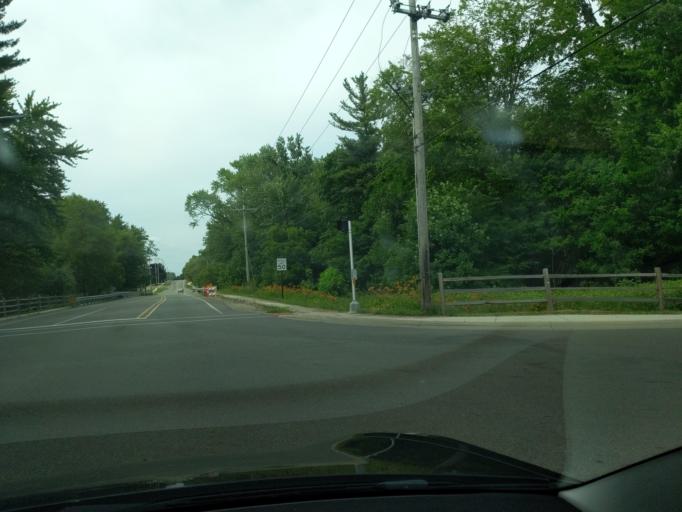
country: US
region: Michigan
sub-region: Clinton County
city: DeWitt
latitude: 42.8235
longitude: -84.6027
